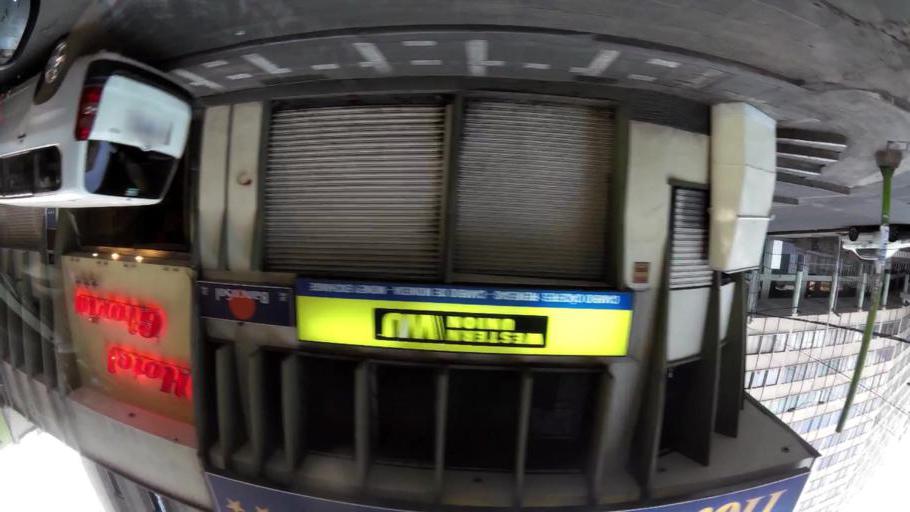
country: BO
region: La Paz
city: La Paz
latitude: -16.4957
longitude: -68.1360
